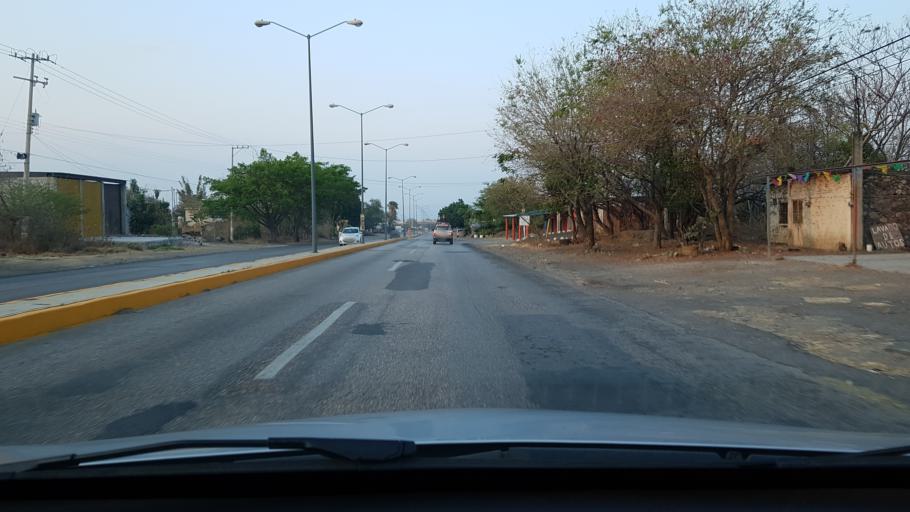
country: MX
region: Morelos
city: Amayuca
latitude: 18.7122
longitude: -98.7976
